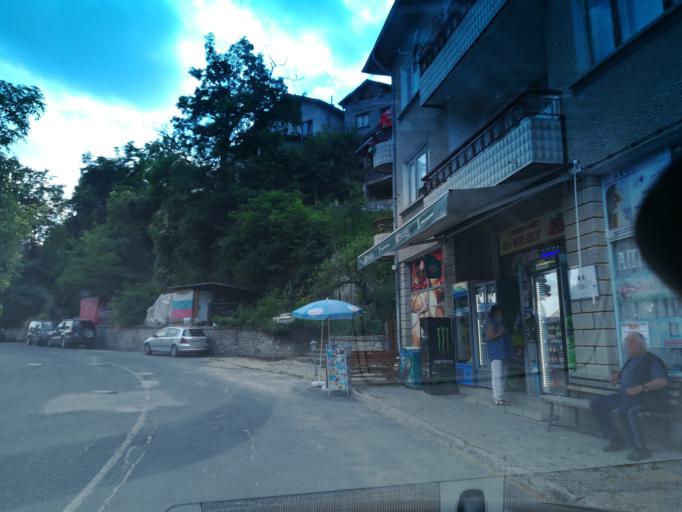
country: BG
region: Smolyan
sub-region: Obshtina Smolyan
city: Smolyan
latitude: 41.6573
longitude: 24.7730
